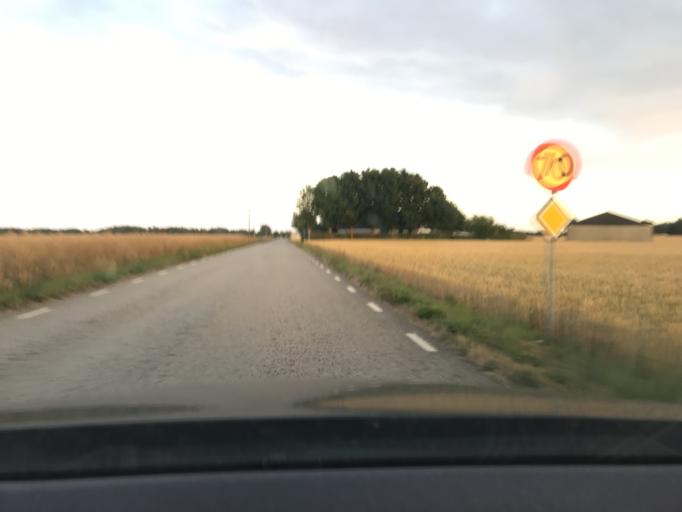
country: SE
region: Skane
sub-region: Simrishamns Kommun
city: Simrishamn
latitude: 55.4416
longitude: 14.2203
